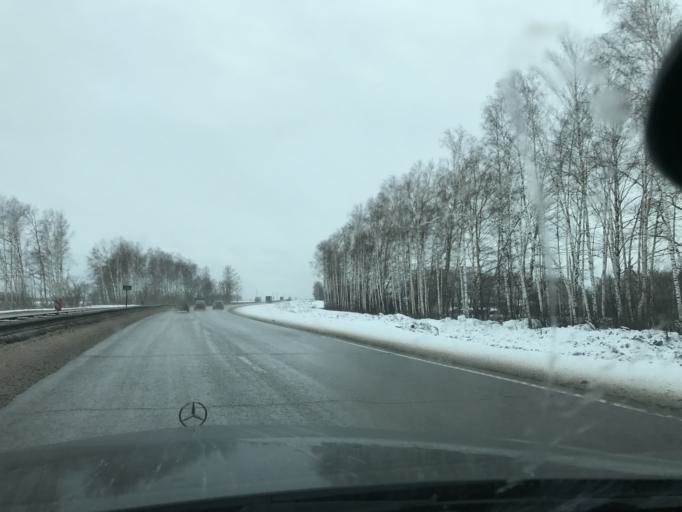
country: RU
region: Vladimir
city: Gorokhovets
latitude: 56.1743
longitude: 42.6509
